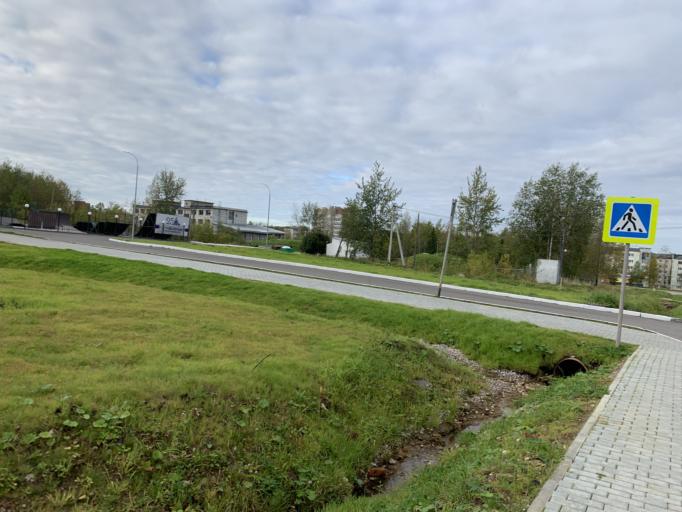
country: RU
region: Perm
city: Gubakha
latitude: 58.8343
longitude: 57.5608
